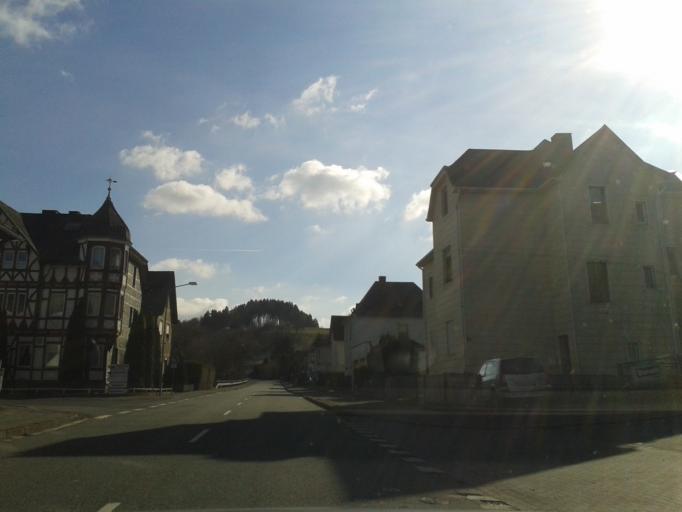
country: DE
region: Hesse
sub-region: Regierungsbezirk Giessen
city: Breidenbach
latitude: 50.8214
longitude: 8.4466
